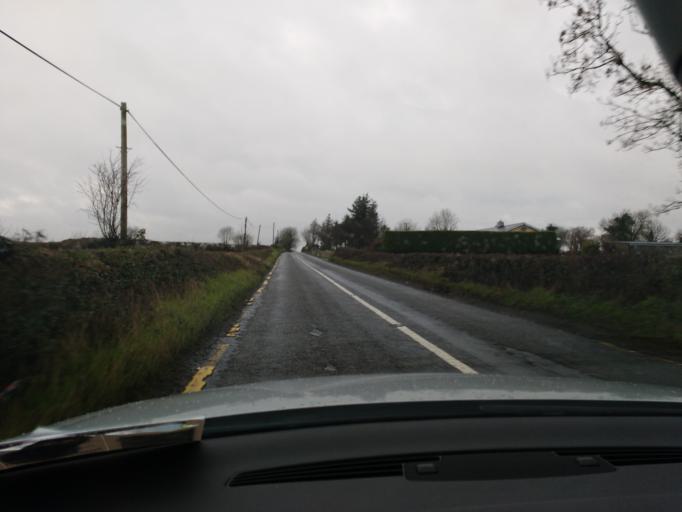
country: IE
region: Munster
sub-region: North Tipperary
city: Nenagh
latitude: 52.8431
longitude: -8.1431
